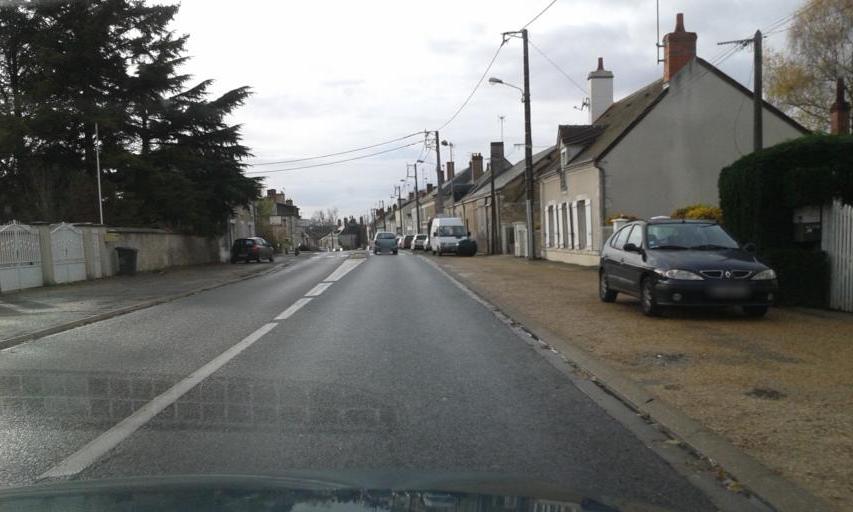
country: FR
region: Centre
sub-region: Departement du Loiret
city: Saint-Ay
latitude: 47.8607
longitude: 1.7575
